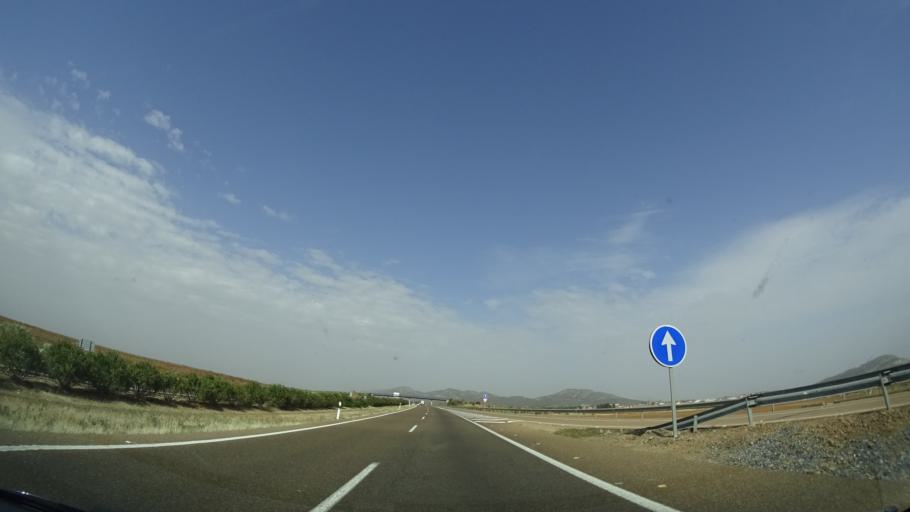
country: ES
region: Extremadura
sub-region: Provincia de Badajoz
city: Almendralejo
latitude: 38.7757
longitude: -6.3809
